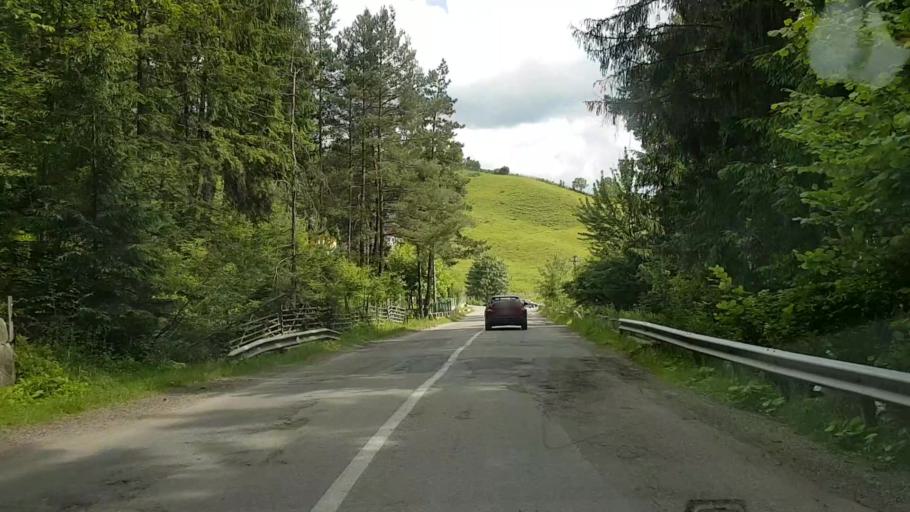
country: RO
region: Neamt
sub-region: Comuna Hangu
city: Hangu
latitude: 47.0052
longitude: 26.0977
